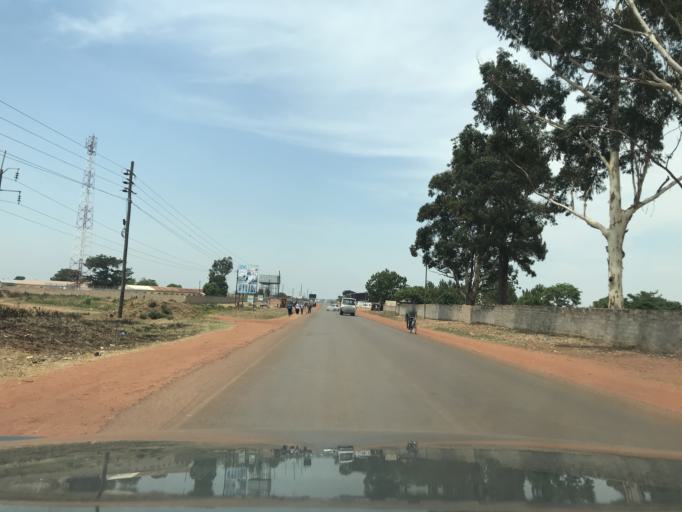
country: ZM
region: Northern
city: Kasama
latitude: -10.2071
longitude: 31.1741
